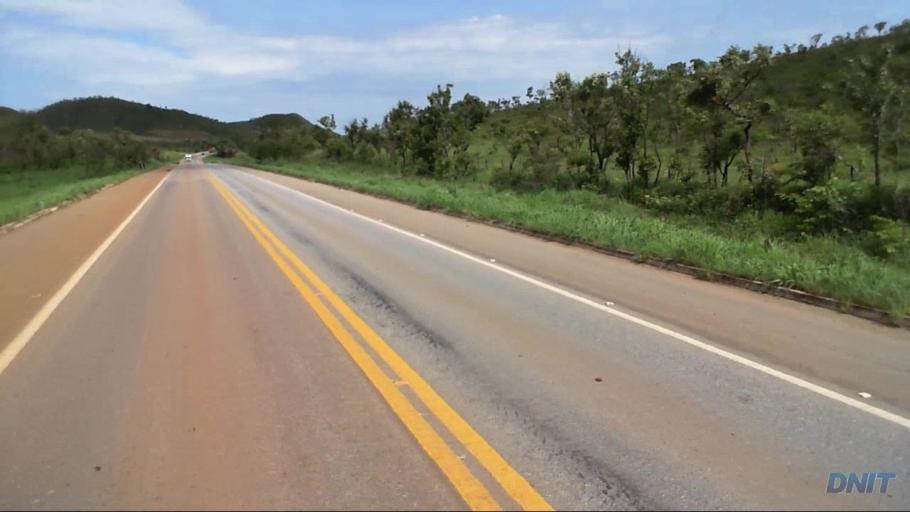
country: BR
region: Goias
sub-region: Barro Alto
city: Barro Alto
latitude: -15.1802
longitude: -48.7889
